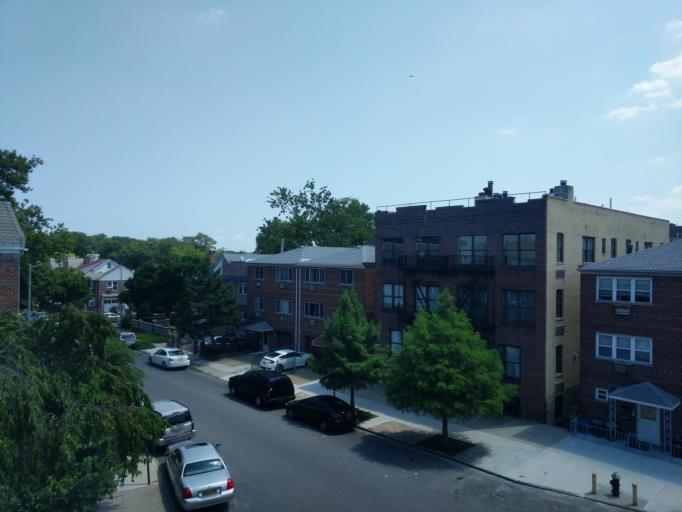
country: US
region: New York
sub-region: Bronx
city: The Bronx
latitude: 40.8492
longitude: -73.8304
